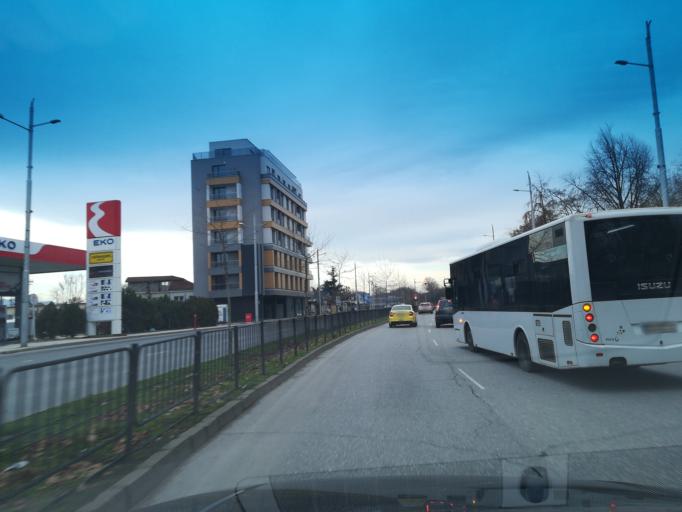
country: BG
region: Plovdiv
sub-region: Obshtina Plovdiv
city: Plovdiv
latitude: 42.1333
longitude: 24.7320
